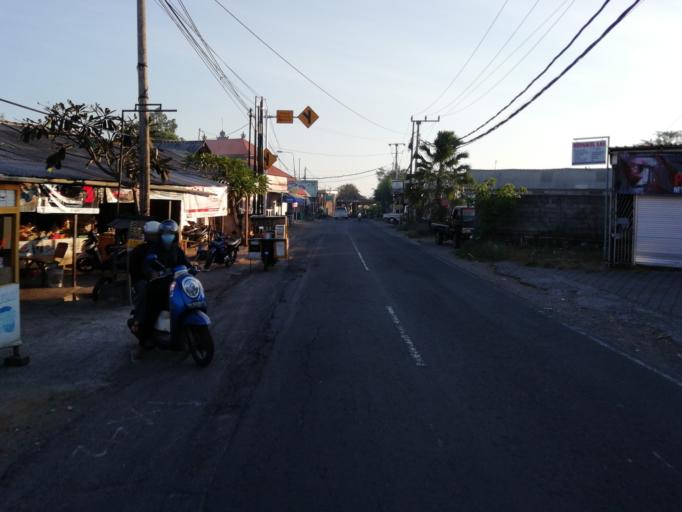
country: ID
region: Bali
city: Jimbaran
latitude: -8.8275
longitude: 115.1813
